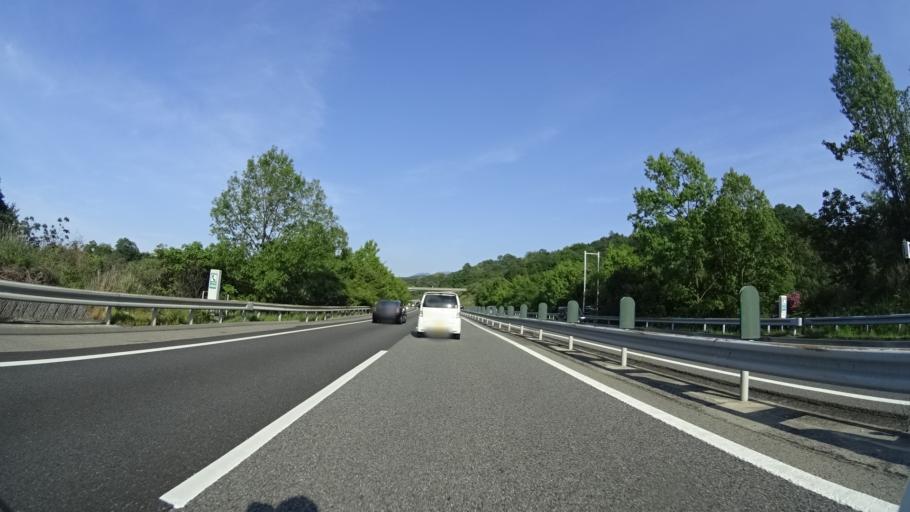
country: JP
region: Ehime
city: Saijo
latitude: 33.8830
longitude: 133.1168
